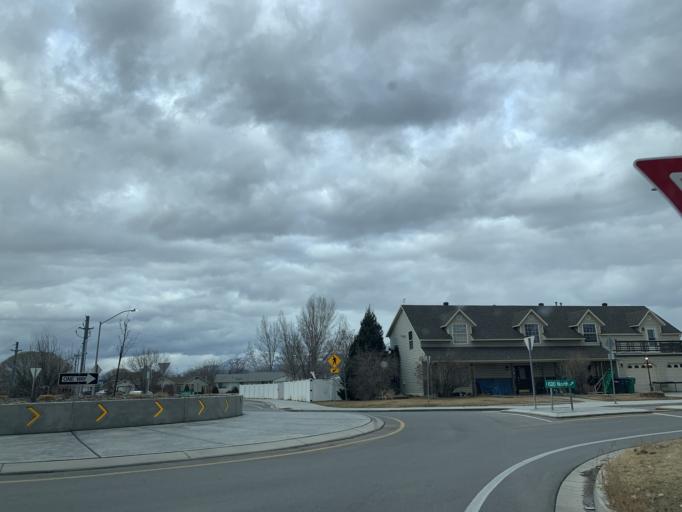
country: US
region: Utah
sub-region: Utah County
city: Provo
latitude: 40.2423
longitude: -111.7098
